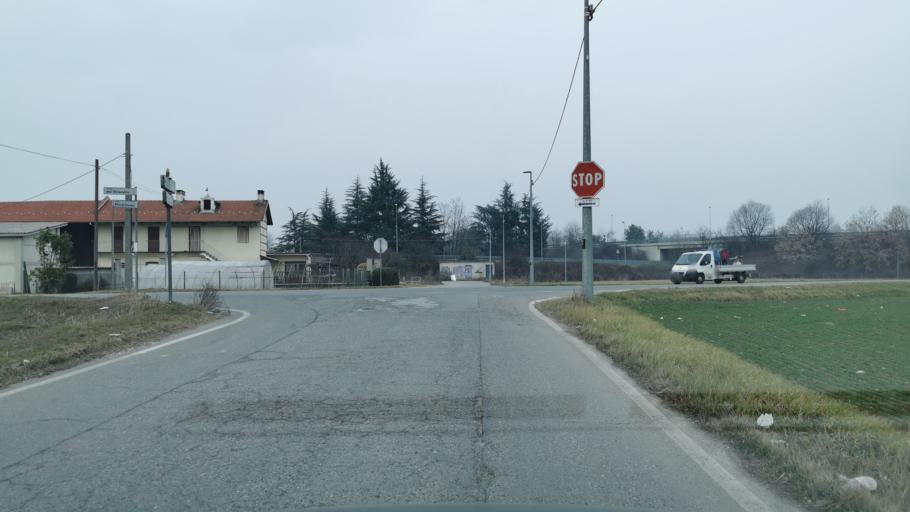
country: IT
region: Piedmont
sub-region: Provincia di Torino
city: Borgaro Torinese
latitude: 45.1250
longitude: 7.6934
